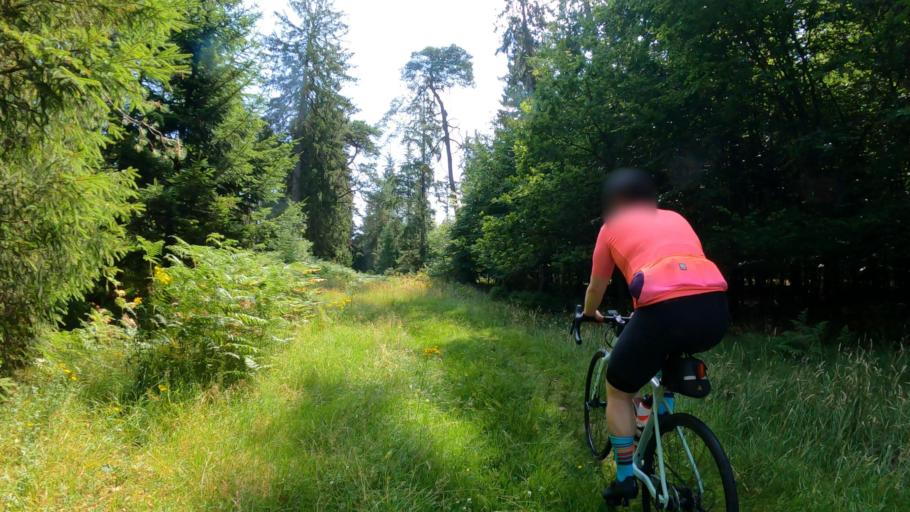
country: DE
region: Schleswig-Holstein
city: Bark
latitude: 53.9334
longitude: 10.1939
